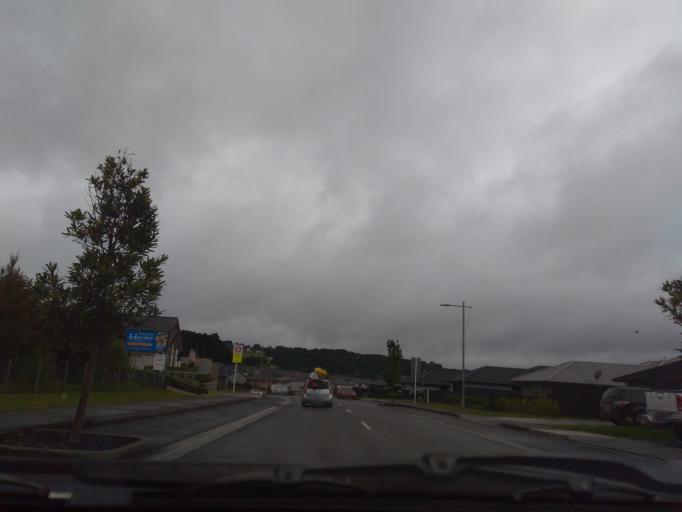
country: NZ
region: Northland
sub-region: Whangarei
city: Whangarei
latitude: -35.6792
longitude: 174.3169
